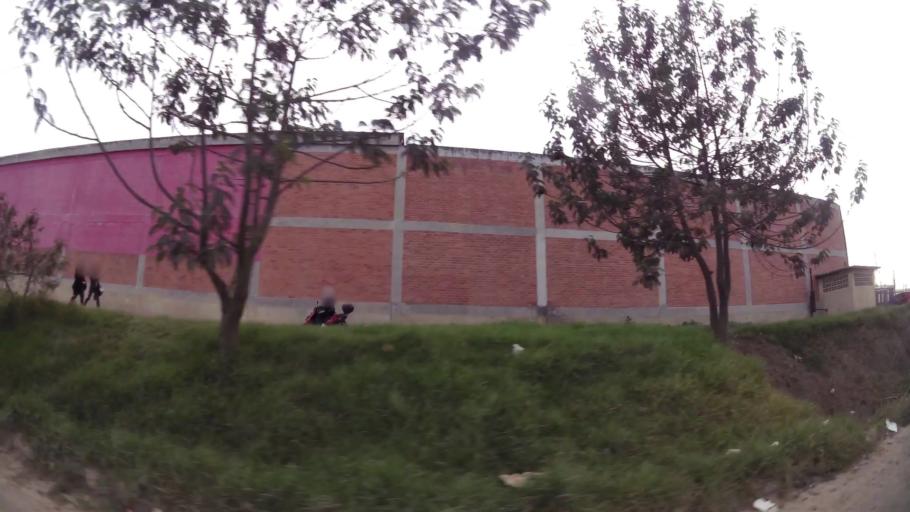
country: CO
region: Cundinamarca
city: Funza
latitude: 4.6970
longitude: -74.1791
